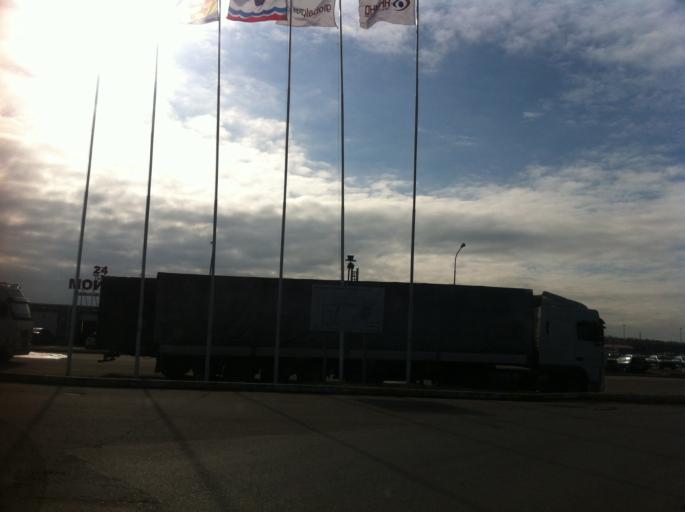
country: RU
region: Leningrad
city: Yanino Vtoroye
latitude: 59.9454
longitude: 30.5749
